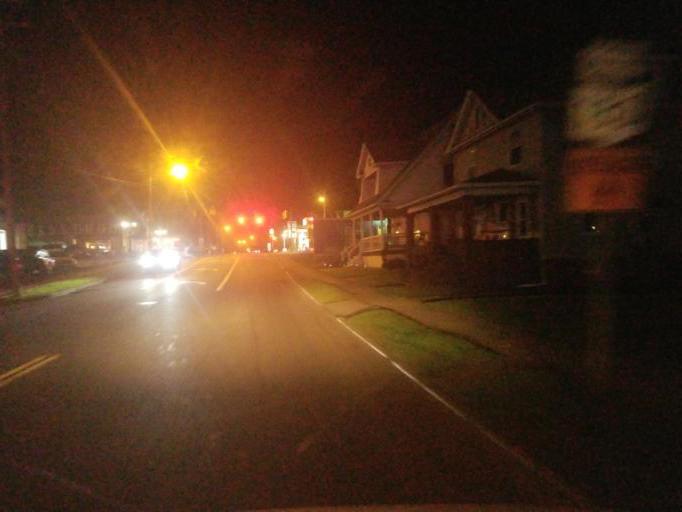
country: US
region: Ohio
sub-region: Stark County
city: Minerva
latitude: 40.7302
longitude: -81.1028
